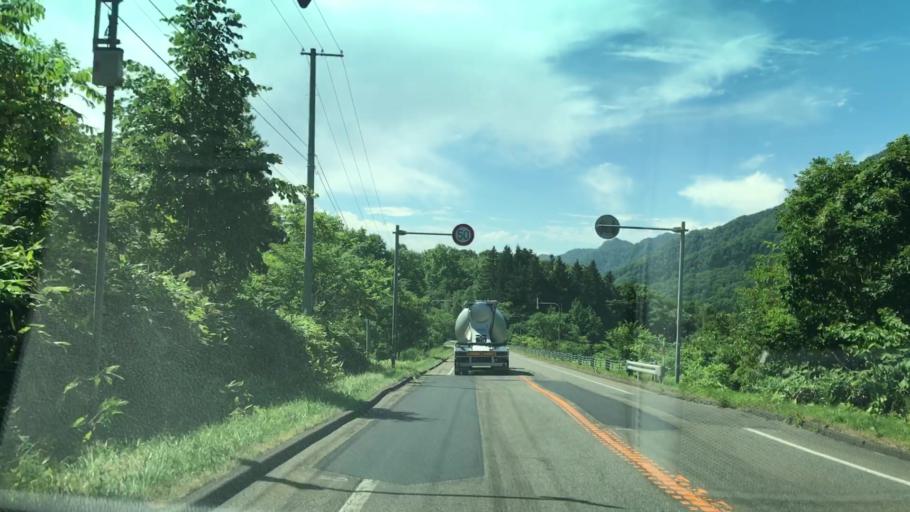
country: JP
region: Hokkaido
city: Shimo-furano
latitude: 42.8931
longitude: 142.4356
